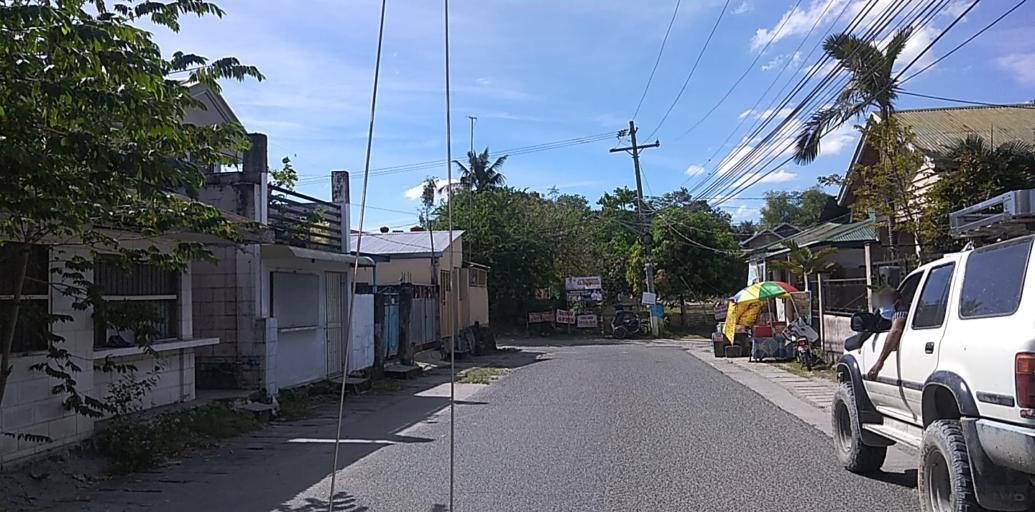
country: PH
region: Central Luzon
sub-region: Province of Pampanga
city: Porac
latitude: 15.0712
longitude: 120.5416
